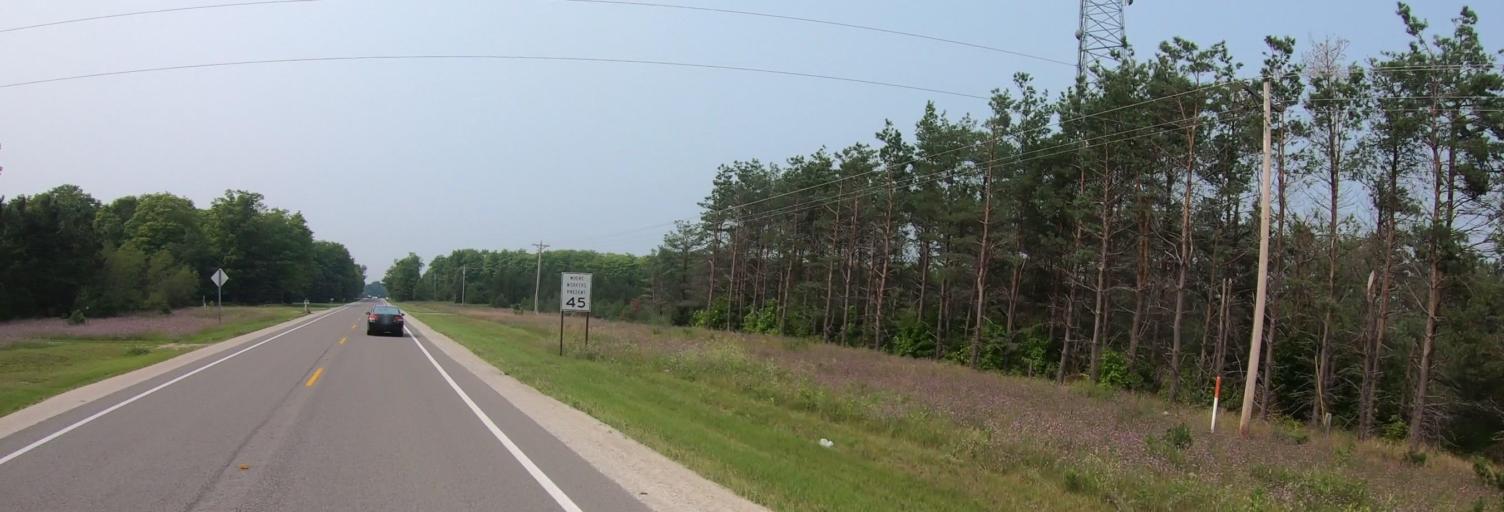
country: US
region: Michigan
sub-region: Chippewa County
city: Sault Ste. Marie
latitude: 46.0232
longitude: -84.0740
